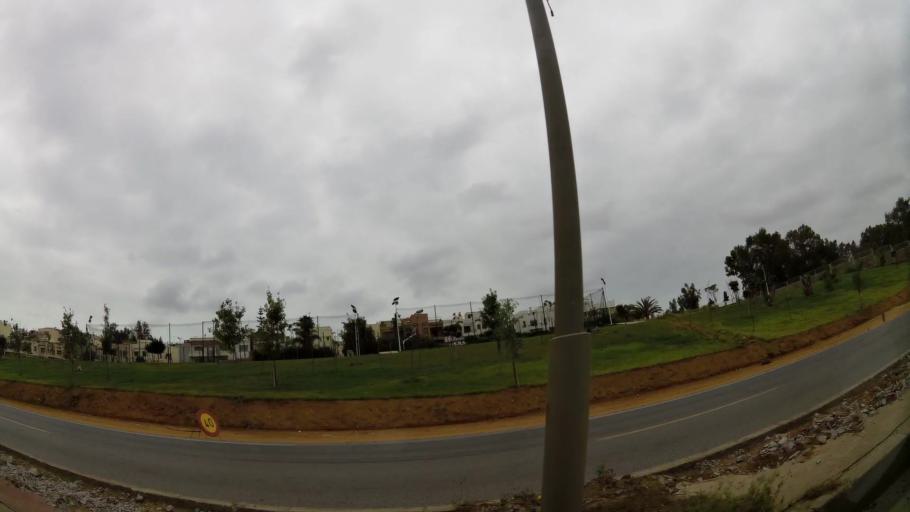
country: MA
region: Rabat-Sale-Zemmour-Zaer
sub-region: Rabat
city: Rabat
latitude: 33.9714
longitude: -6.8153
